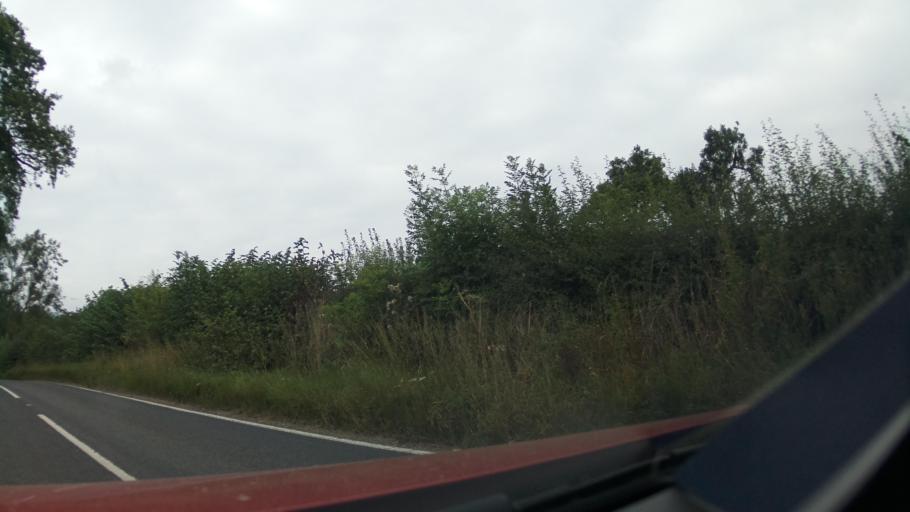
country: GB
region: England
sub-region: Derbyshire
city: Wirksworth
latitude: 53.0255
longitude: -1.5579
